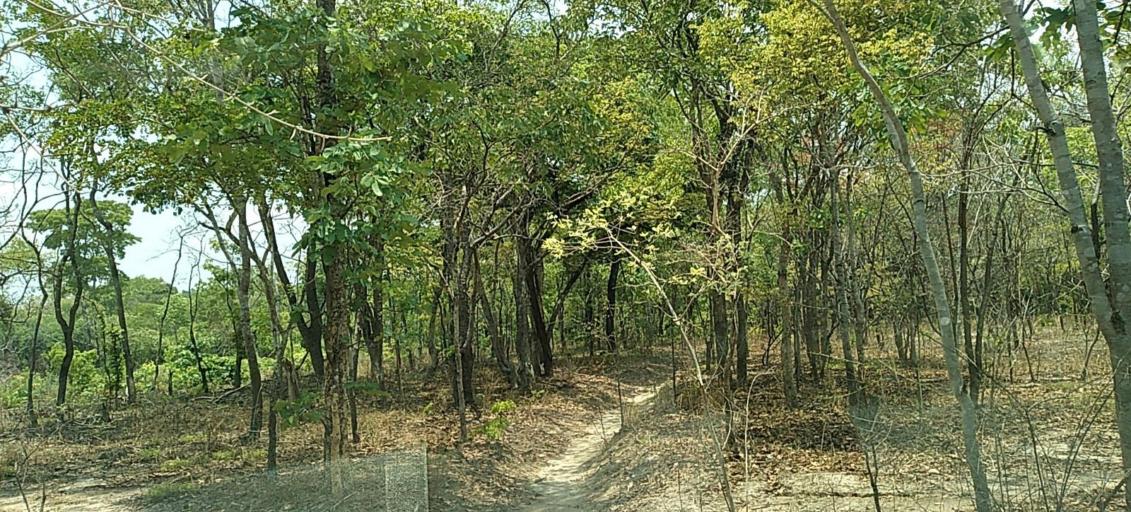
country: ZM
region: Copperbelt
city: Luanshya
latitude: -13.1600
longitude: 28.1838
